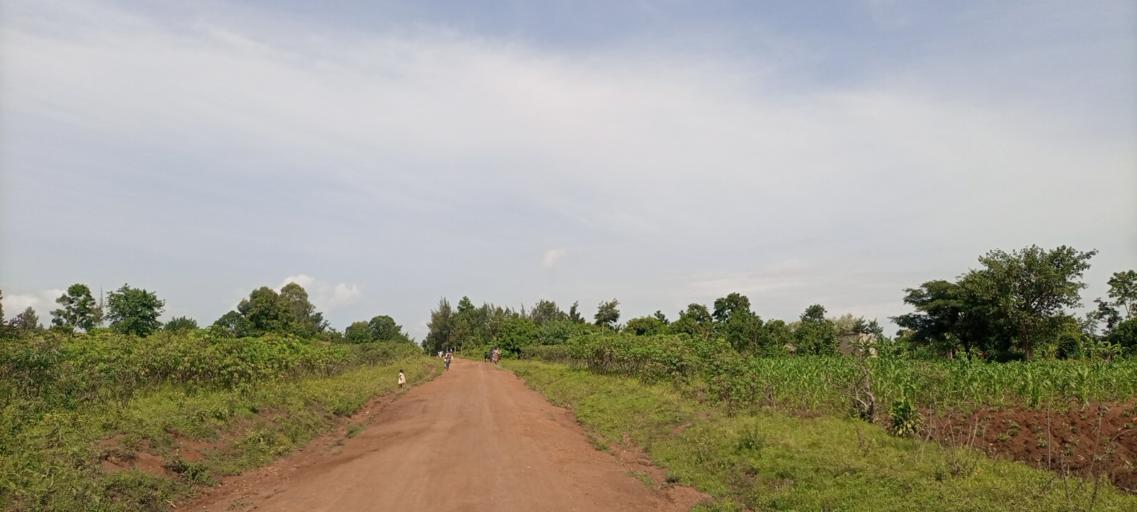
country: UG
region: Eastern Region
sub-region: Mbale District
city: Mbale
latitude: 1.1354
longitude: 34.0566
